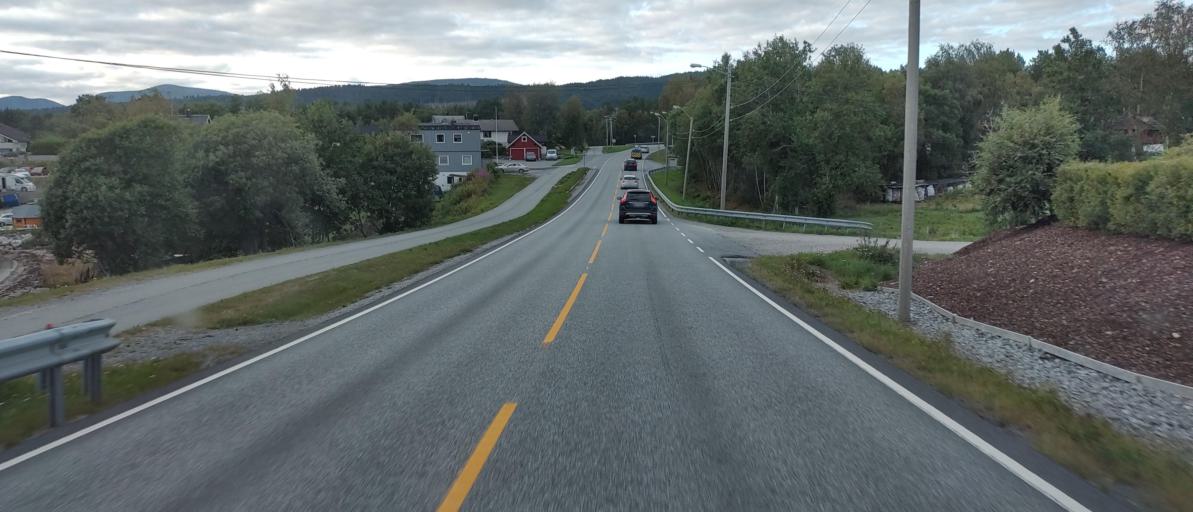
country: NO
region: More og Romsdal
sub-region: Molde
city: Hjelset
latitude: 62.7165
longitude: 7.4279
